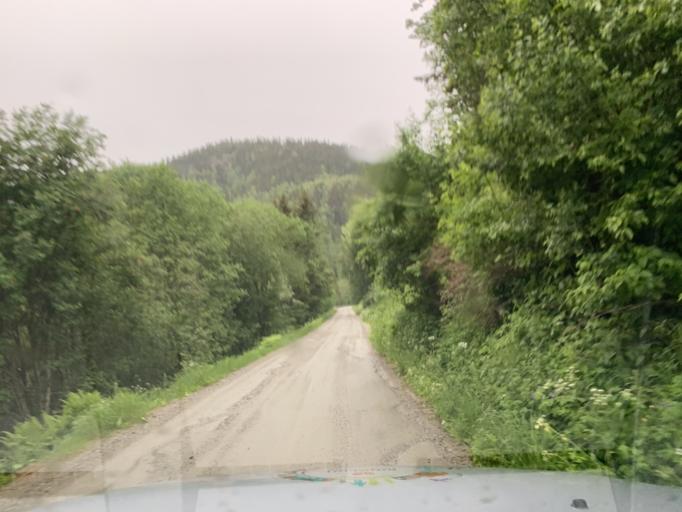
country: NO
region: Oppland
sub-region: Oyer
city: Tretten
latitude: 61.3908
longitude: 10.2771
